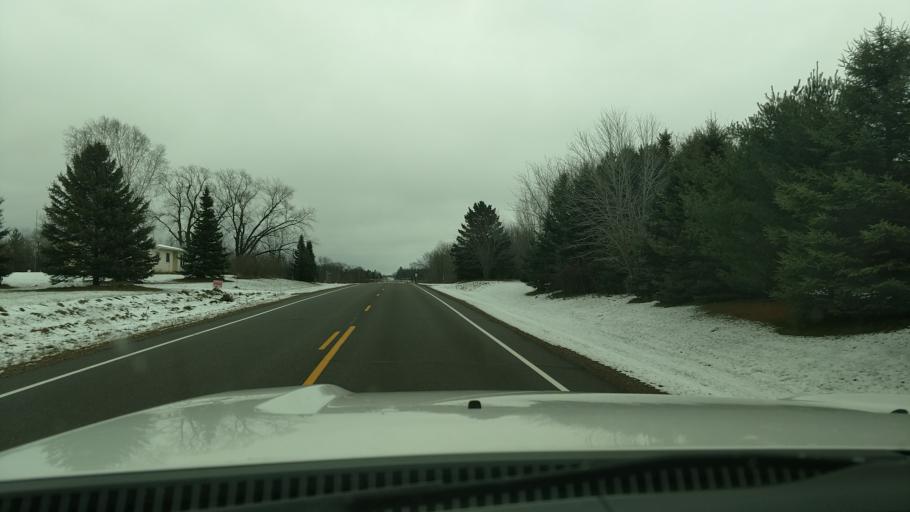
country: US
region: Wisconsin
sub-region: Dunn County
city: Colfax
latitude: 45.1429
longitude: -91.7097
